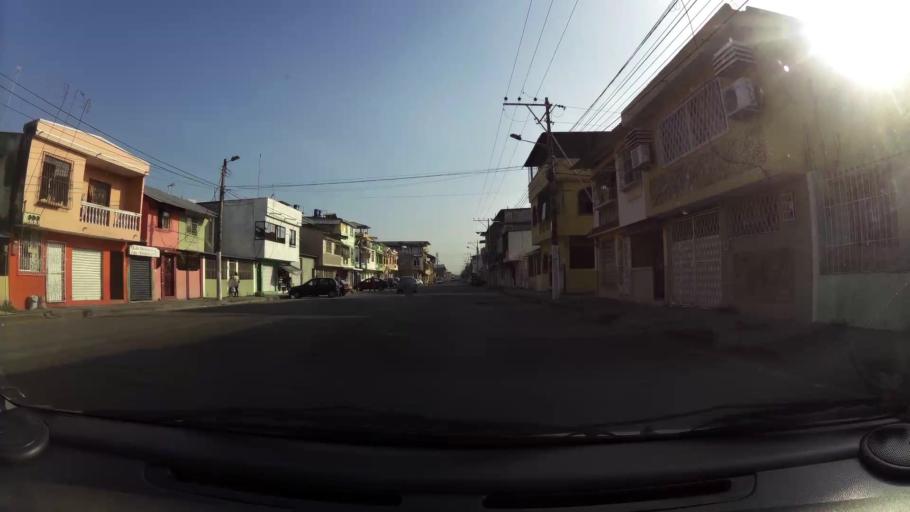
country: EC
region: Guayas
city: Eloy Alfaro
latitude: -2.1865
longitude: -79.8563
